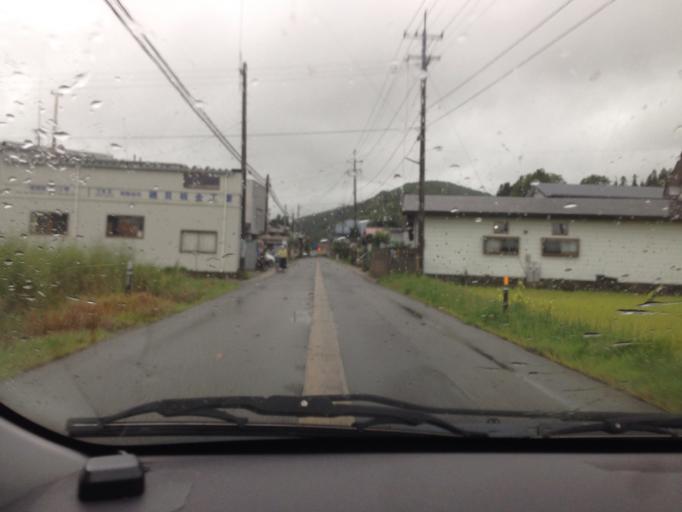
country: JP
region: Fukushima
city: Inawashiro
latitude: 37.3982
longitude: 140.1306
